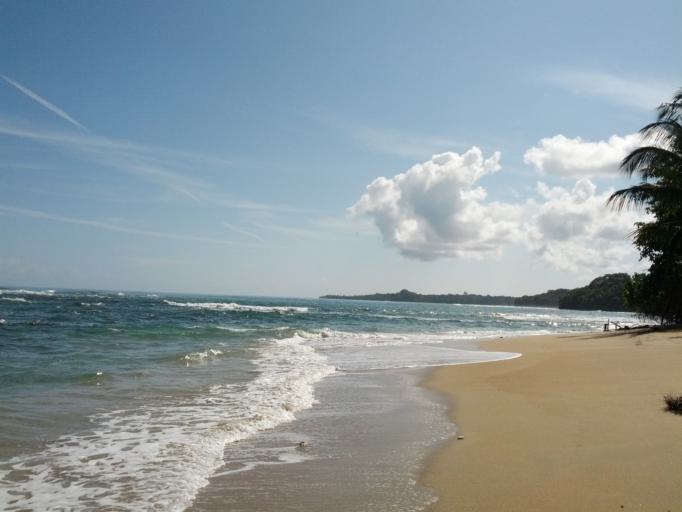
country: PA
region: Bocas del Toro
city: Barranco
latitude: 9.6452
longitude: -82.7197
